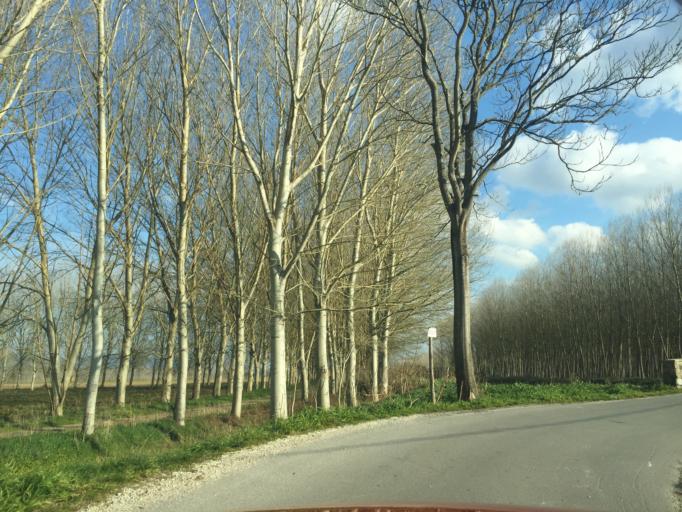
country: IT
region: Tuscany
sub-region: Provincia di Pistoia
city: Anchione
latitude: 43.8069
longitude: 10.7573
